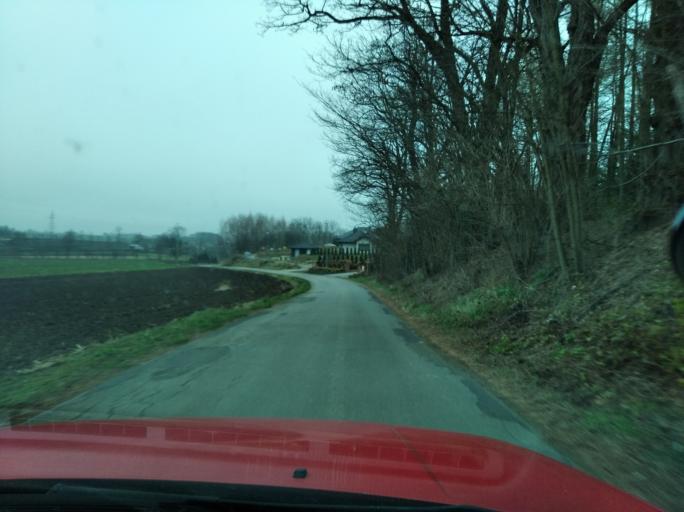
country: PL
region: Subcarpathian Voivodeship
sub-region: Powiat jaroslawski
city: Pawlosiow
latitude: 50.0173
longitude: 22.6287
